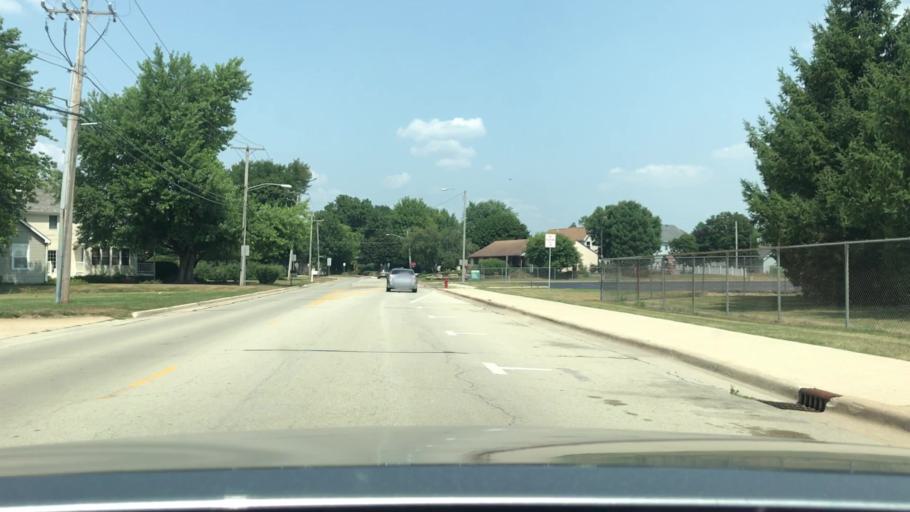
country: US
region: Illinois
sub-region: Will County
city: Plainfield
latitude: 41.6041
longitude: -88.2091
